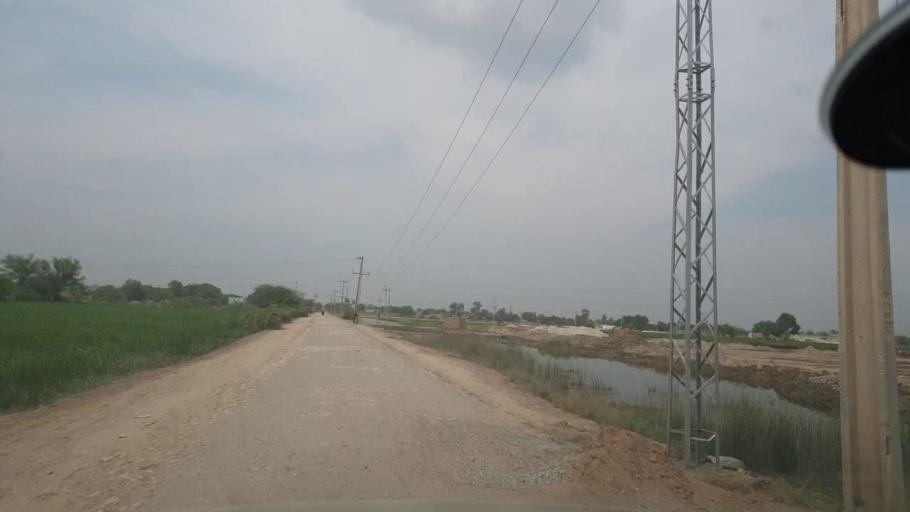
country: PK
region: Sindh
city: Jacobabad
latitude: 28.2596
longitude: 68.4373
